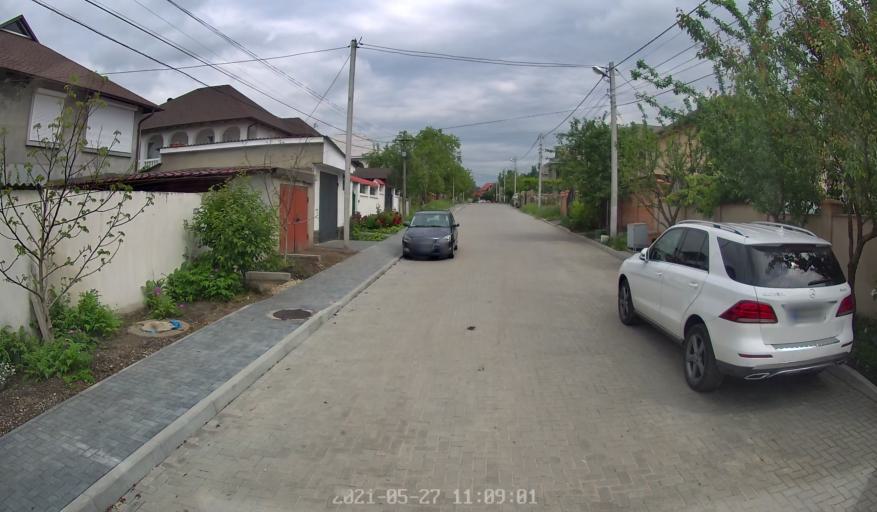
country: MD
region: Chisinau
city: Stauceni
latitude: 47.1002
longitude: 28.8673
